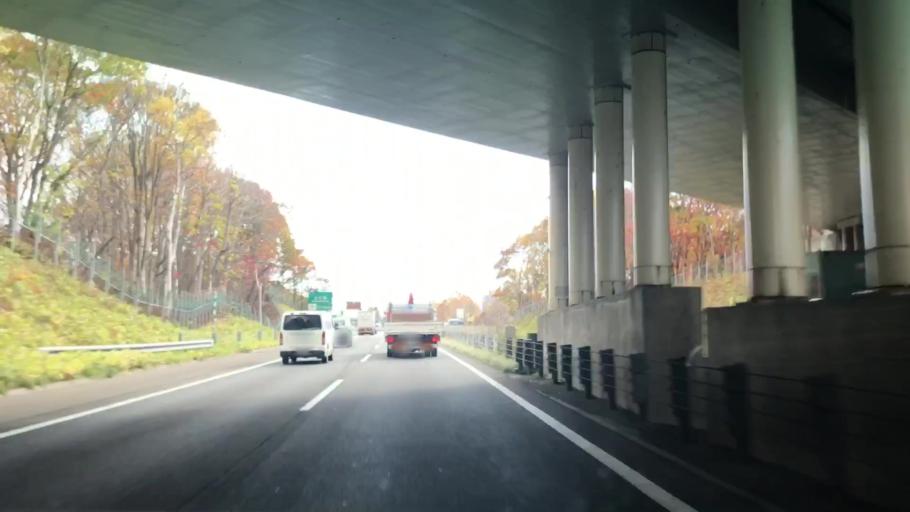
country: JP
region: Hokkaido
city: Kitahiroshima
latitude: 42.9838
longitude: 141.4724
